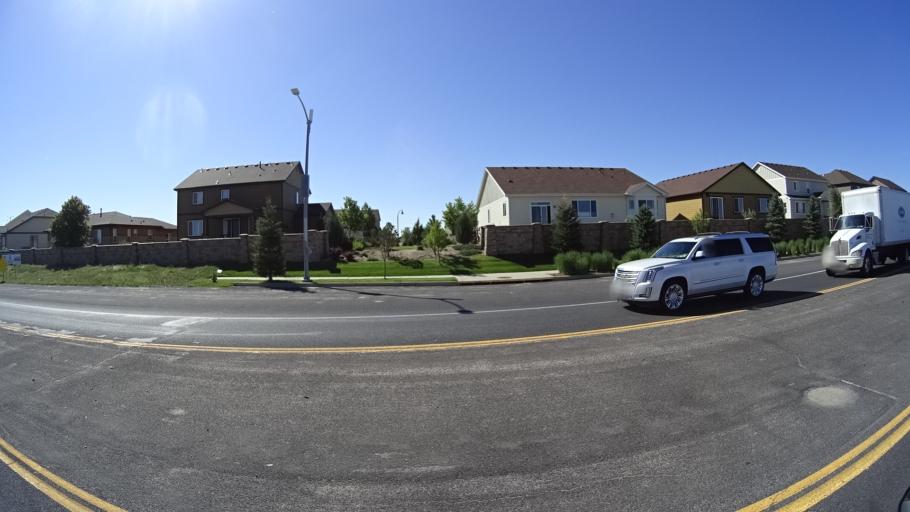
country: US
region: Colorado
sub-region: El Paso County
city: Black Forest
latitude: 38.9370
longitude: -104.6800
